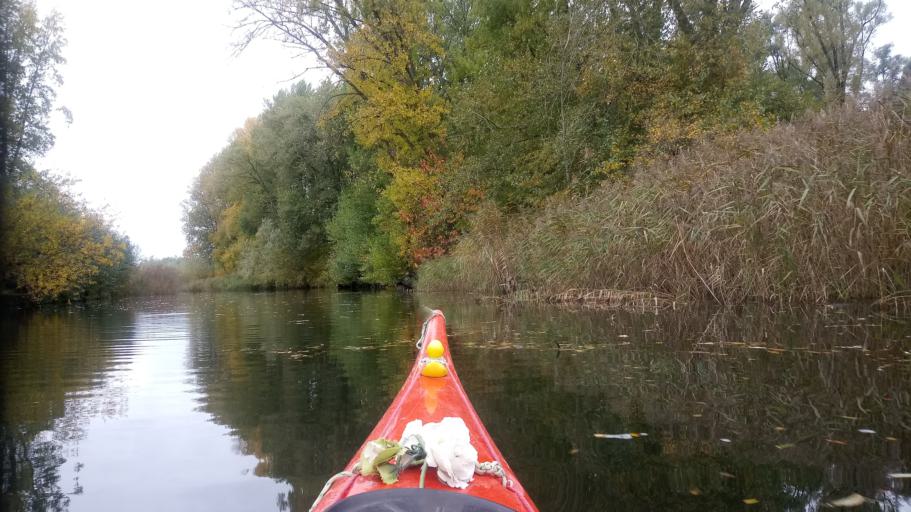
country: NL
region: North Brabant
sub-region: Gemeente Geertruidenberg
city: Geertruidenberg
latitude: 51.7525
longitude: 4.8395
